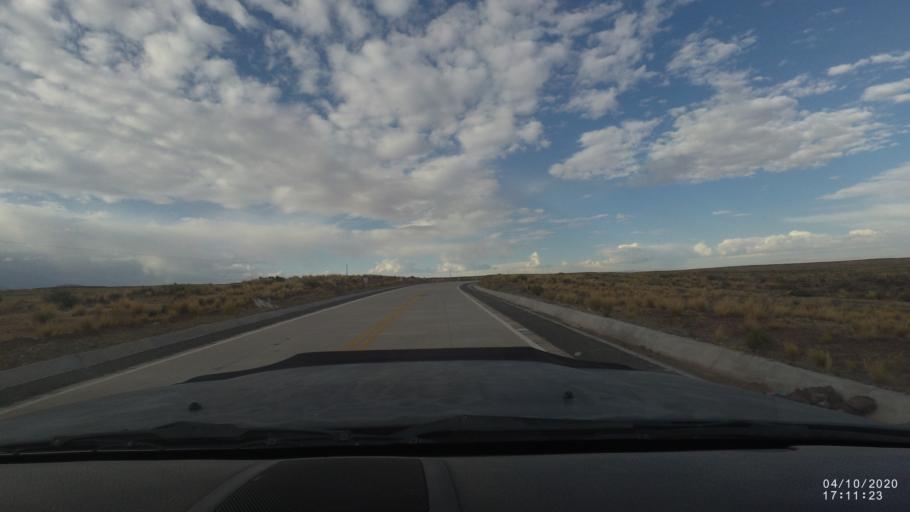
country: BO
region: Oruro
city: Oruro
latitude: -18.3204
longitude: -67.5769
